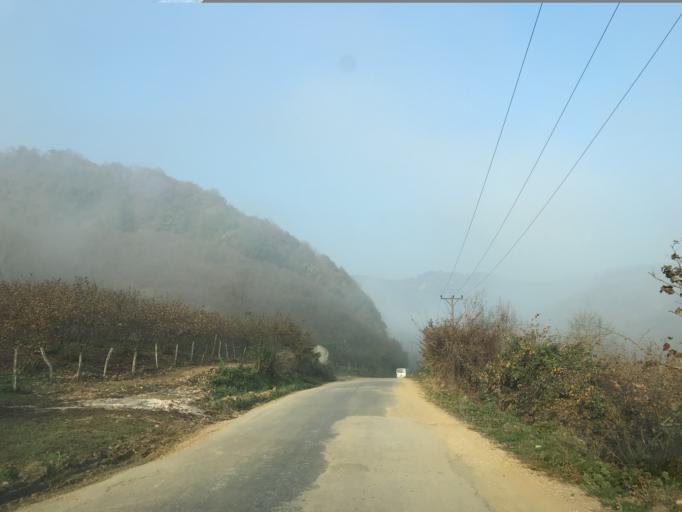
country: TR
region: Duzce
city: Cumayeri
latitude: 40.9132
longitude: 30.9395
